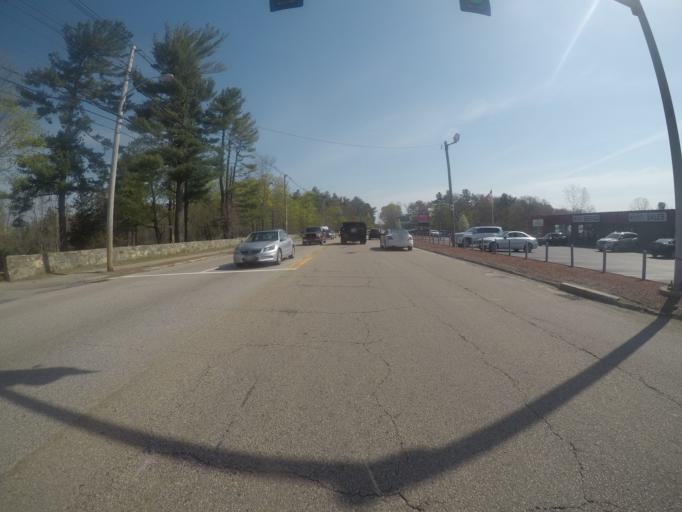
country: US
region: Massachusetts
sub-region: Bristol County
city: Easton
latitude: 42.0546
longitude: -71.0739
